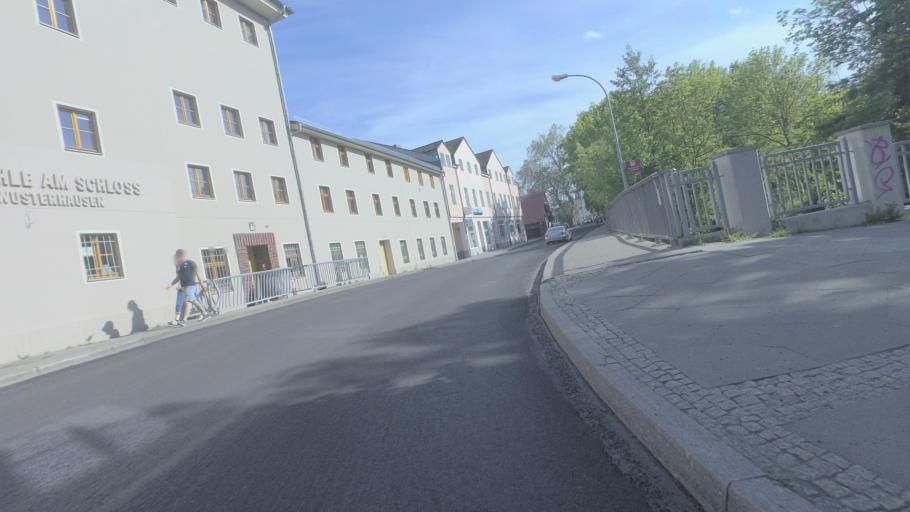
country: DE
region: Brandenburg
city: Konigs Wusterhausen
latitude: 52.2980
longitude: 13.6245
